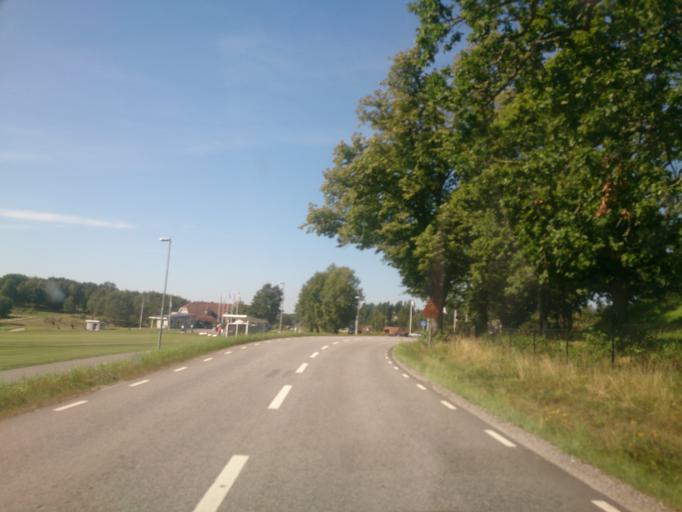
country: SE
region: OEstergoetland
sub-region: Norrkopings Kommun
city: Norrkoping
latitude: 58.4956
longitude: 16.1722
